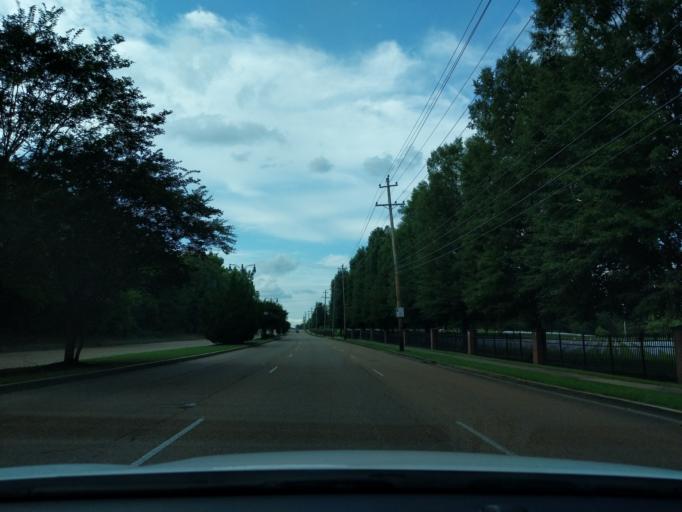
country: US
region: Tennessee
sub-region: Shelby County
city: Germantown
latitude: 35.0360
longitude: -89.7597
